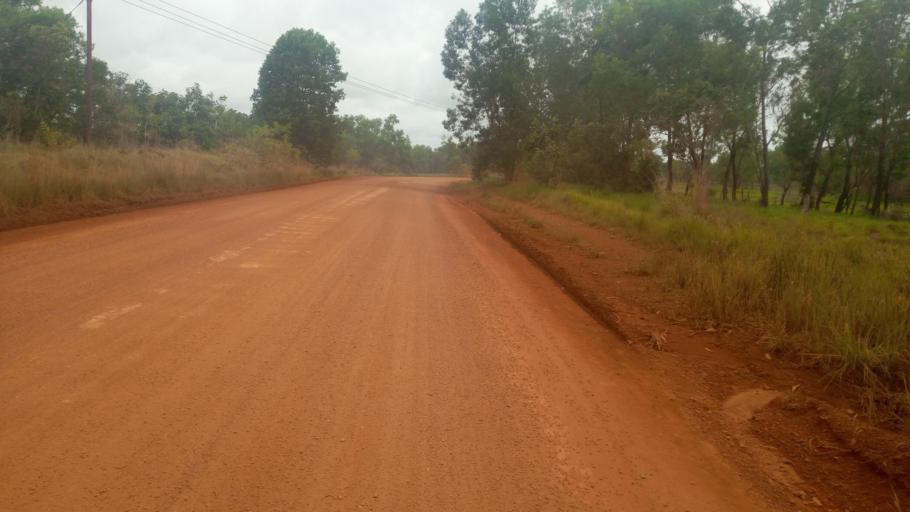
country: SL
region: Southern Province
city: Mogbwemo
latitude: 7.7473
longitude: -12.2925
